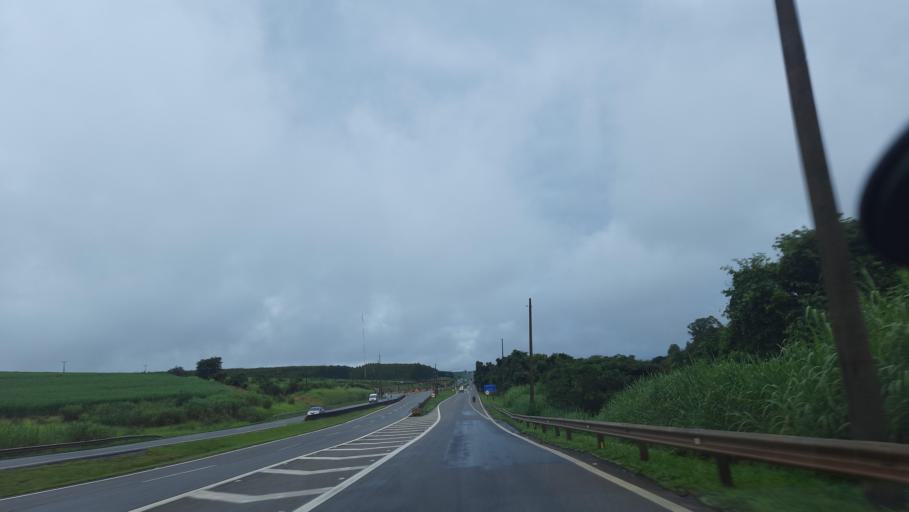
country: BR
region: Sao Paulo
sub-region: Aguai
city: Aguai
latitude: -22.1590
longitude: -46.9932
